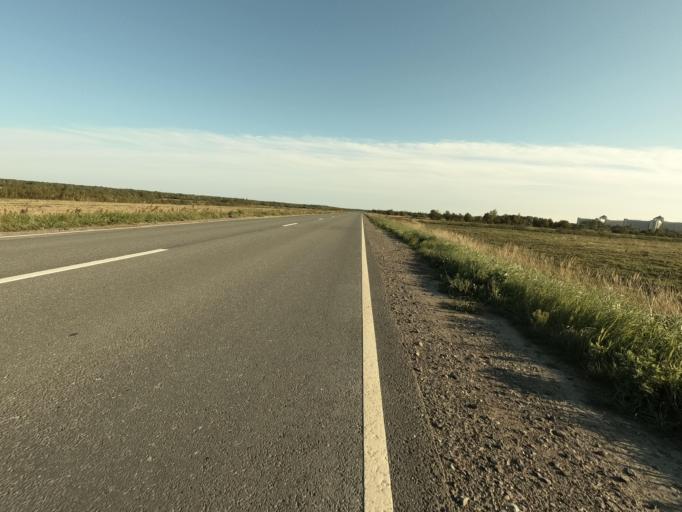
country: RU
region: St.-Petersburg
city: Sapernyy
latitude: 59.7520
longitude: 30.6361
